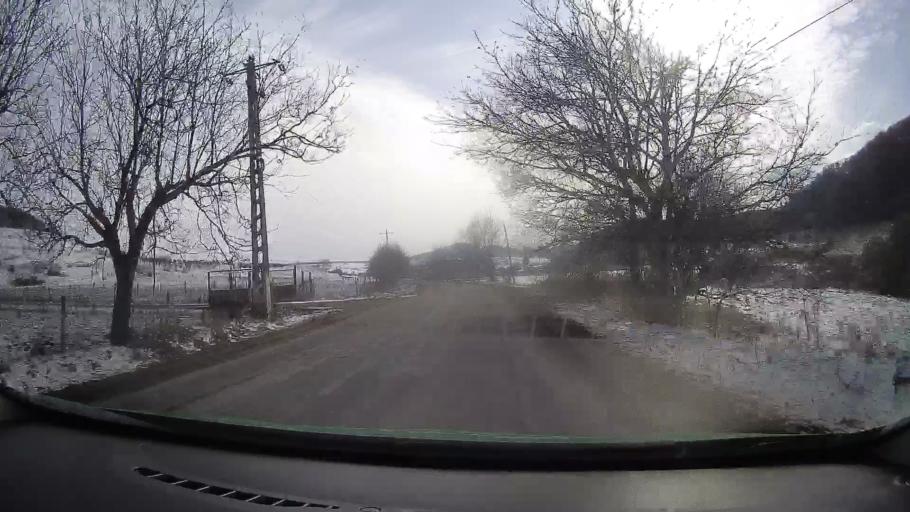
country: RO
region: Mures
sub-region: Comuna Apold
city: Apold
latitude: 46.1369
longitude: 24.8197
